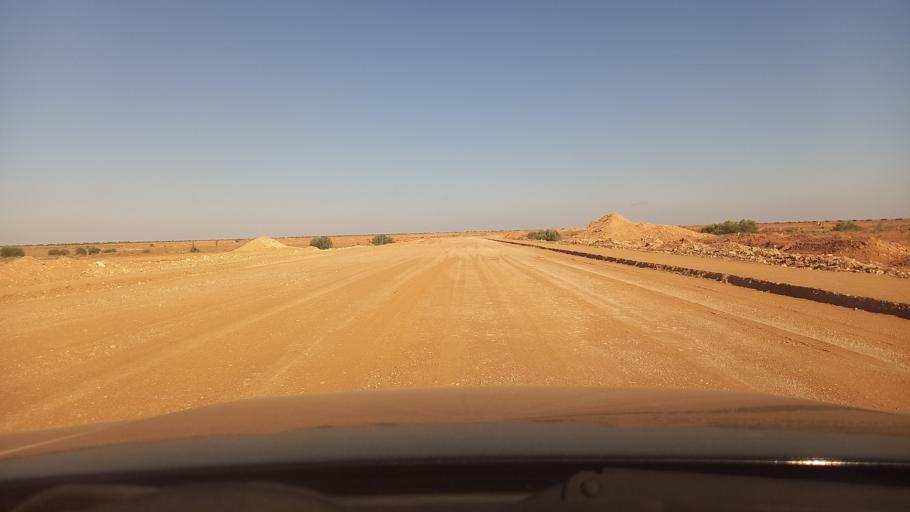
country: TN
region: Madanin
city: Medenine
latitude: 33.1426
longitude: 10.5060
